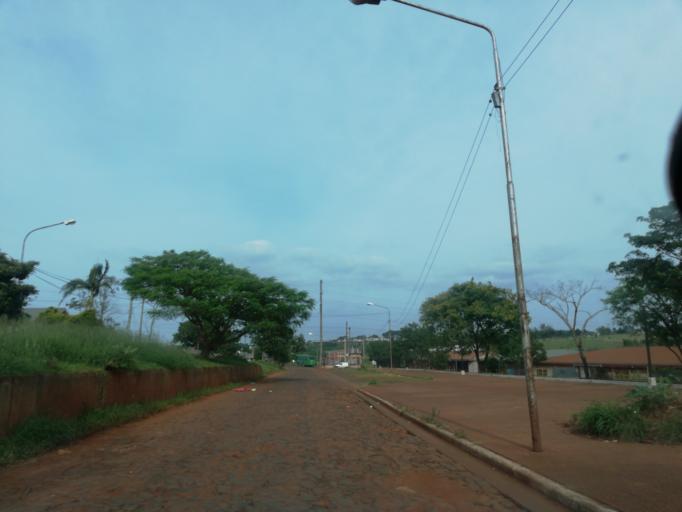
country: AR
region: Misiones
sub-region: Departamento de Capital
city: Posadas
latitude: -27.4359
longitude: -55.9138
